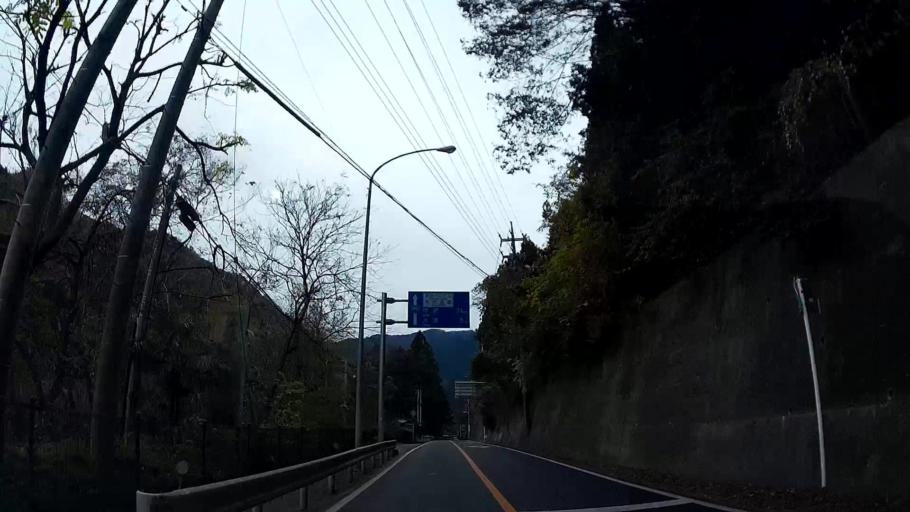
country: JP
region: Saitama
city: Chichibu
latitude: 35.9613
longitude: 138.9740
